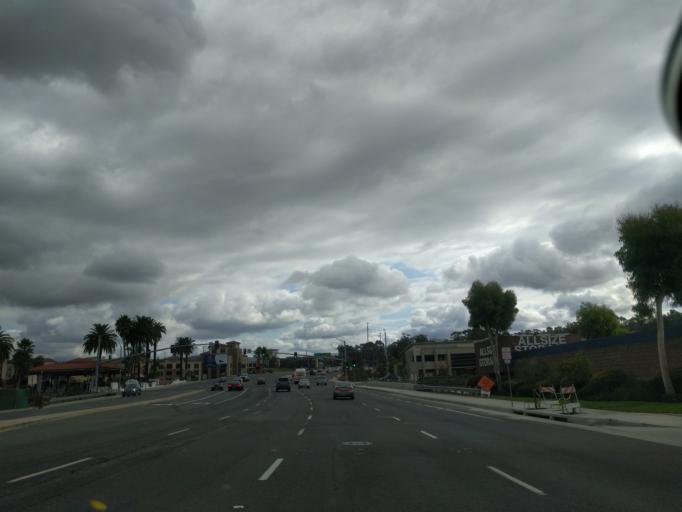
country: US
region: California
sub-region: Orange County
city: Mission Viejo
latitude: 33.5574
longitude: -117.6773
